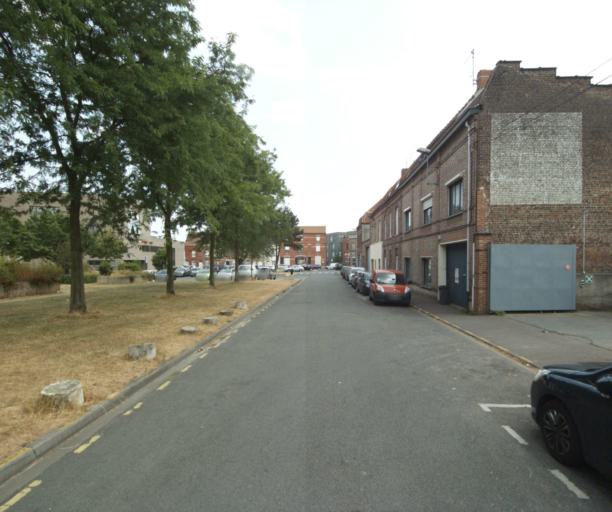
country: FR
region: Nord-Pas-de-Calais
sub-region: Departement du Nord
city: Tourcoing
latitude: 50.7260
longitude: 3.1463
